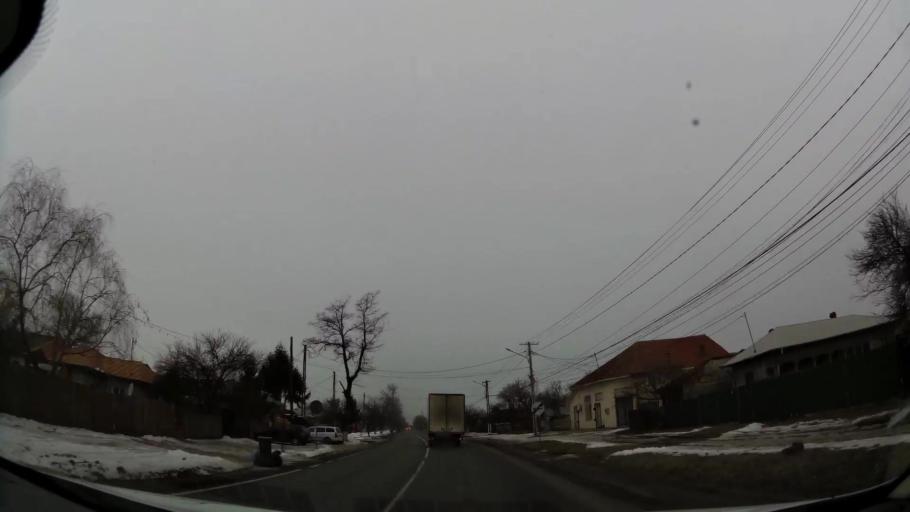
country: RO
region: Dambovita
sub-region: Comuna Tartasesti
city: Baldana
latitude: 44.6151
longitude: 25.7637
